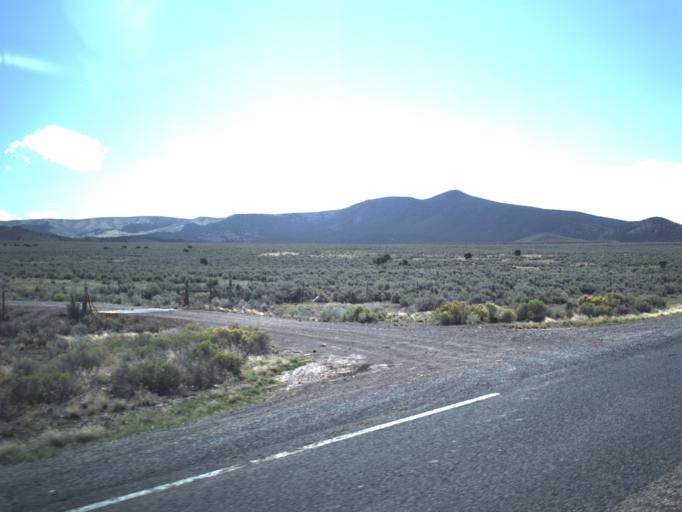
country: US
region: Utah
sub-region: Beaver County
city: Milford
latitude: 38.1957
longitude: -112.9347
